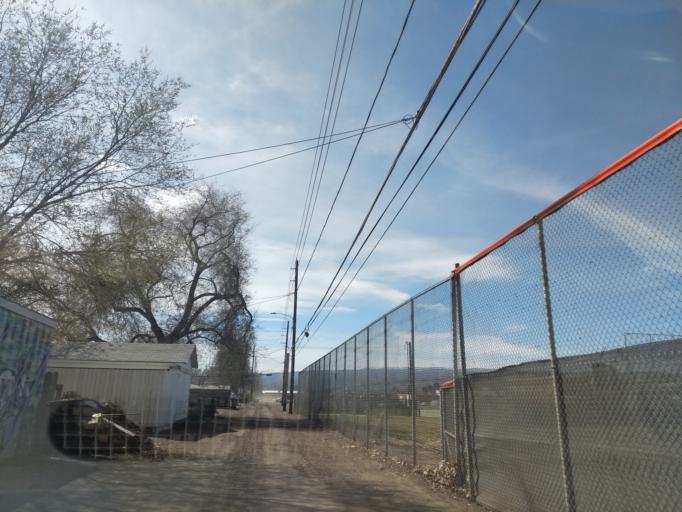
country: US
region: Colorado
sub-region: Mesa County
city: Grand Junction
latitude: 39.0822
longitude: -108.5617
